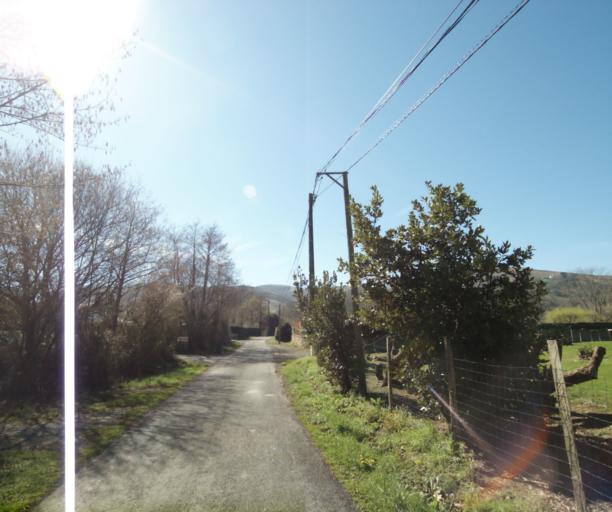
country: FR
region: Aquitaine
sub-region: Departement des Pyrenees-Atlantiques
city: Urrugne
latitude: 43.3414
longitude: -1.6943
